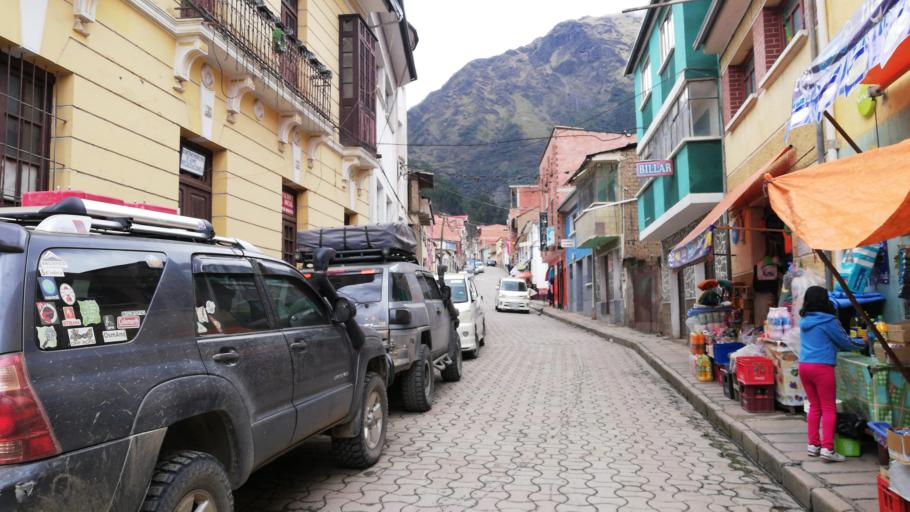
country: BO
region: La Paz
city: Quime
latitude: -16.9799
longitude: -67.2158
